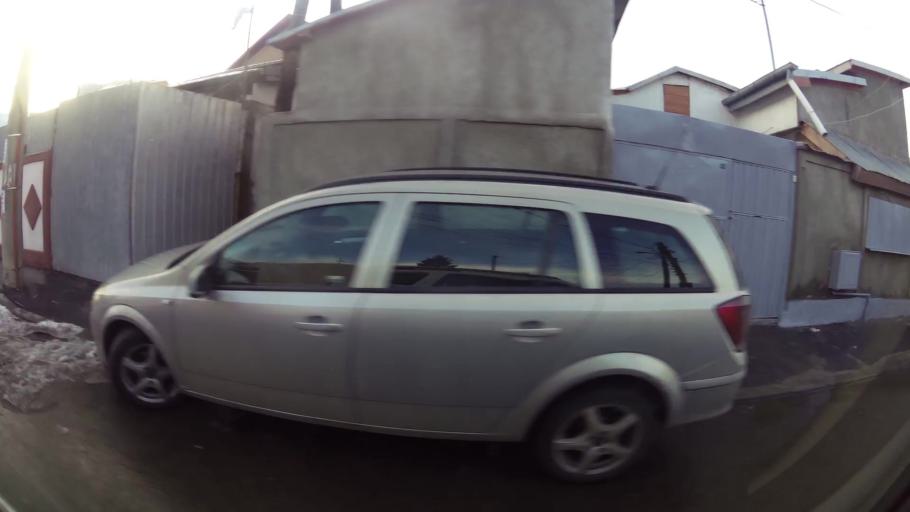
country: RO
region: Bucuresti
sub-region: Municipiul Bucuresti
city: Bucuresti
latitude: 44.3936
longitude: 26.0770
